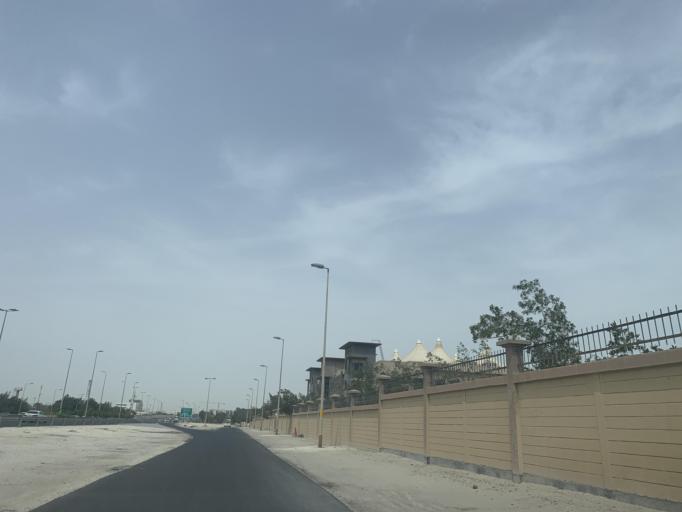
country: BH
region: Northern
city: Madinat `Isa
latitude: 26.1578
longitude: 50.5469
